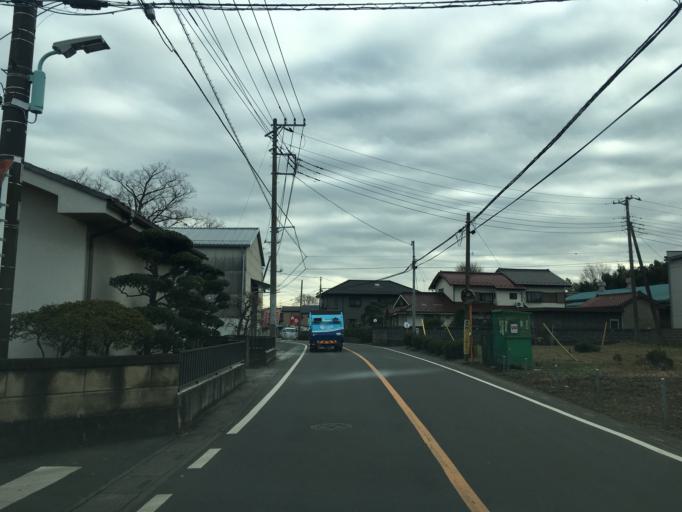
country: JP
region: Saitama
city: Sayama
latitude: 35.7942
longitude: 139.3990
